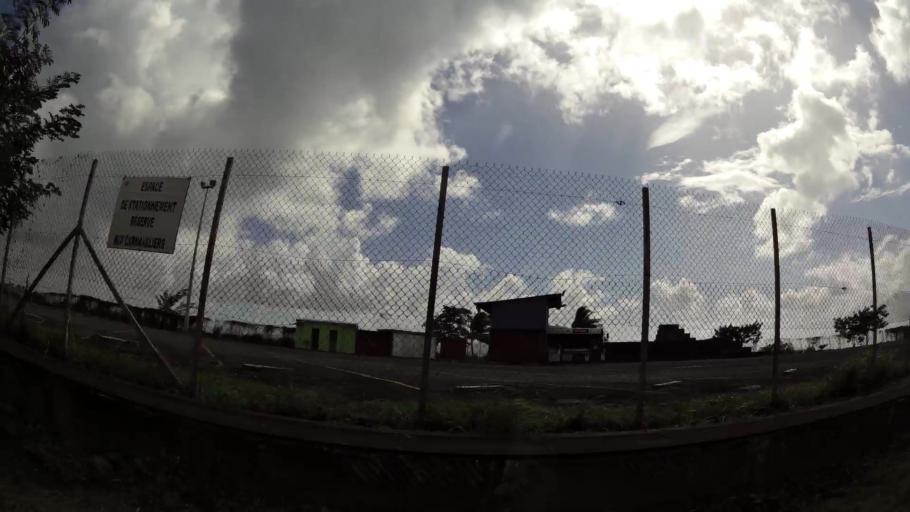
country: MQ
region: Martinique
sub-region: Martinique
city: Fort-de-France
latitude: 14.6016
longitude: -61.0776
